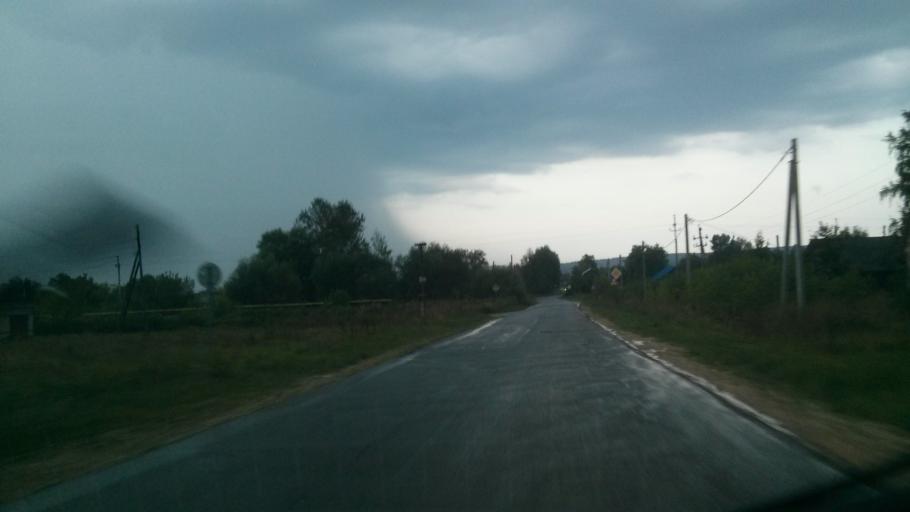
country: RU
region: Nizjnij Novgorod
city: Shimorskoye
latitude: 55.3350
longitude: 41.9200
